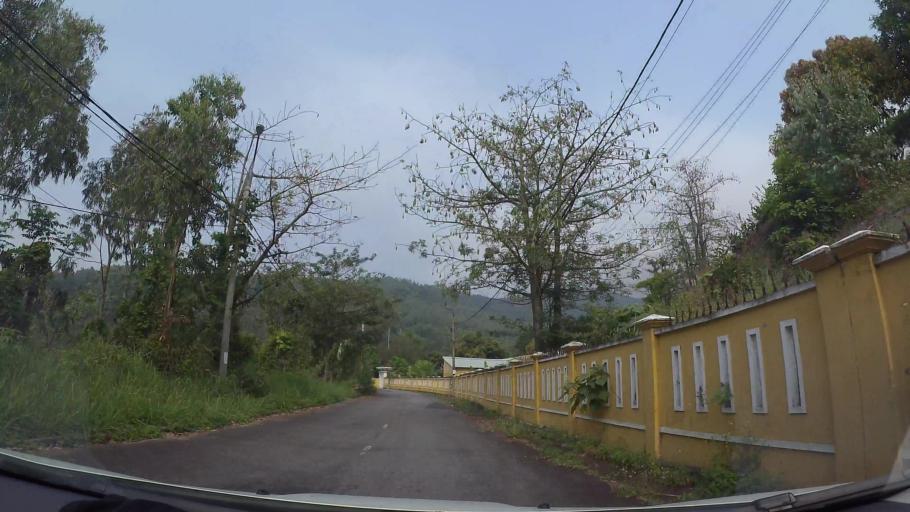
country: VN
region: Da Nang
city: Son Tra
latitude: 16.1096
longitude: 108.2595
